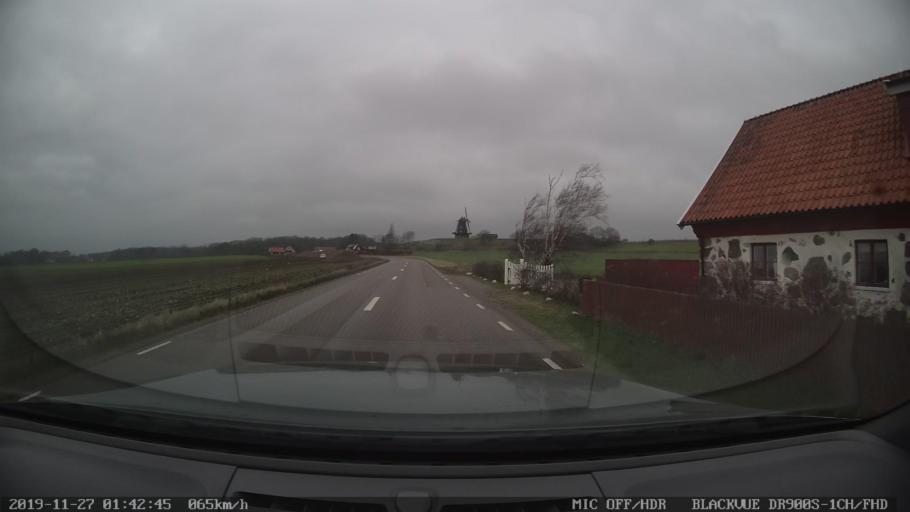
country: SE
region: Skane
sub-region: Hoganas Kommun
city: Hoganas
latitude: 56.2536
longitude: 12.5340
